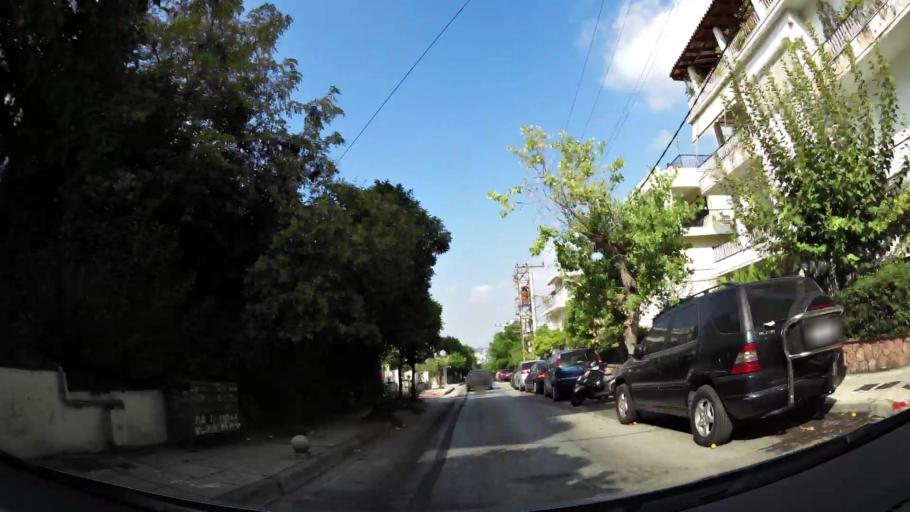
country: GR
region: Attica
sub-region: Nomarchia Athinas
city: Cholargos
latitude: 37.9944
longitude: 23.7957
